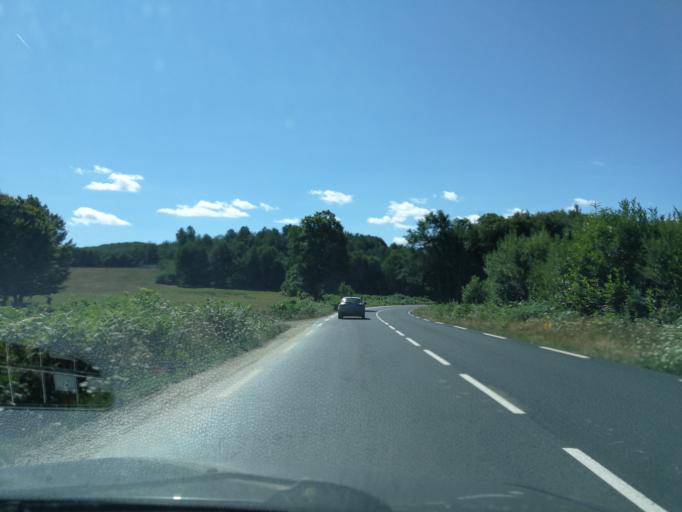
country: FR
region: Limousin
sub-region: Departement de la Correze
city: Sainte-Fortunade
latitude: 45.1677
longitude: 1.7575
